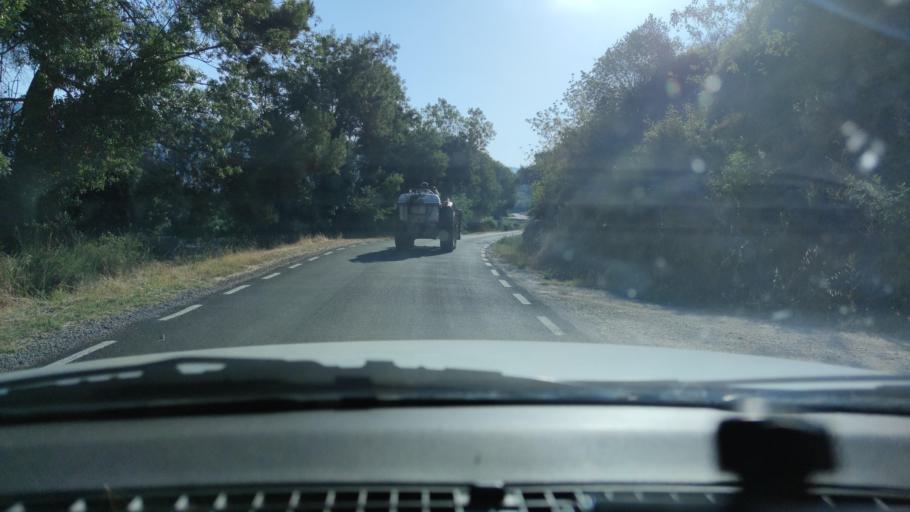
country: ES
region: Catalonia
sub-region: Provincia de Lleida
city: Camarasa
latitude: 41.8689
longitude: 0.8677
